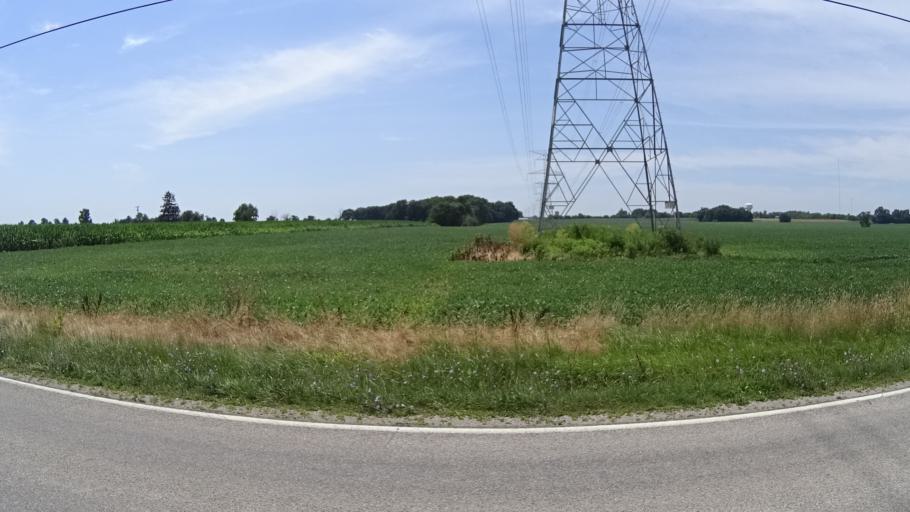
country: US
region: Ohio
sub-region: Erie County
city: Sandusky
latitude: 41.3858
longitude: -82.7706
